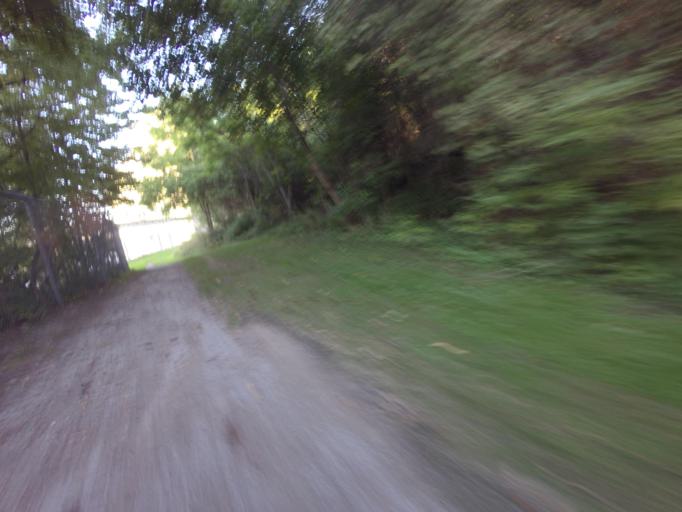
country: CA
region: Ontario
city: Goderich
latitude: 43.7439
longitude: -81.7214
